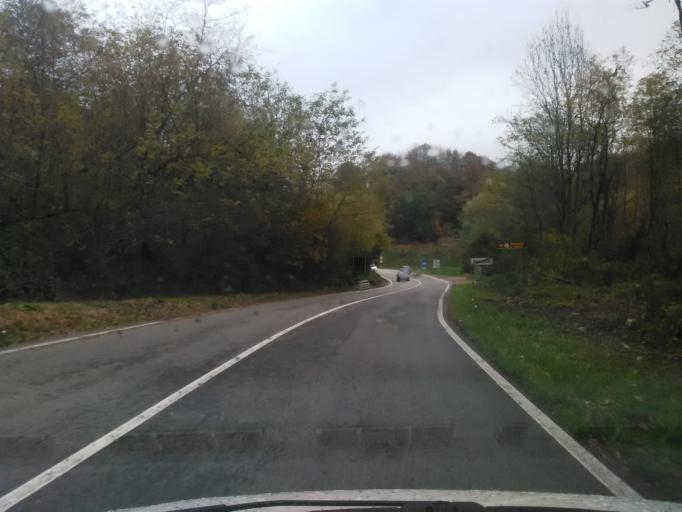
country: IT
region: Piedmont
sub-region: Provincia di Vercelli
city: Borgosesia
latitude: 45.7163
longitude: 8.2983
